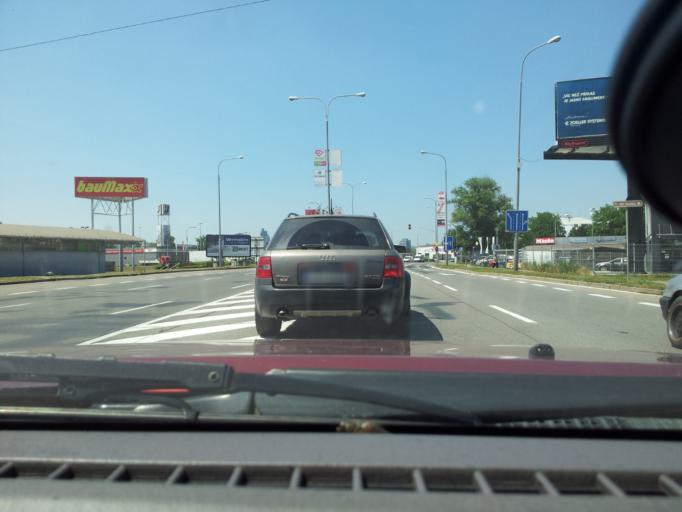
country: CZ
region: South Moravian
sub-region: Mesto Brno
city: Brno
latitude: 49.1662
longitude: 16.6296
